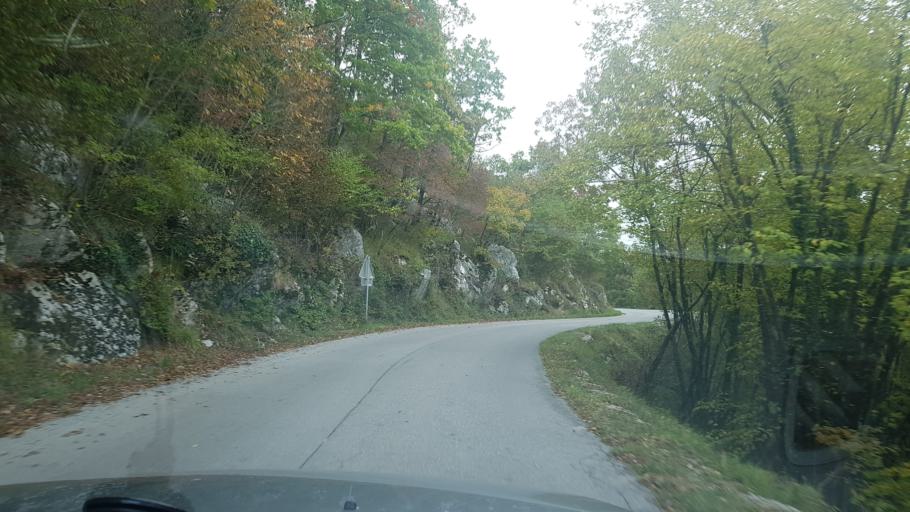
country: HR
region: Istarska
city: Buzet
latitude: 45.5111
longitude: 13.9649
